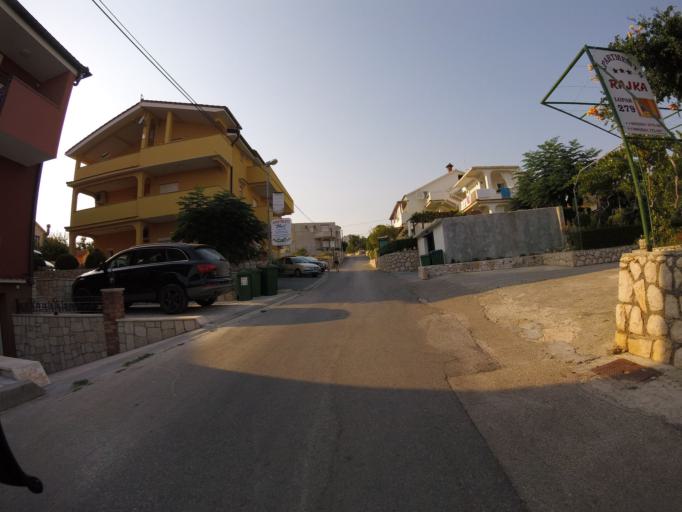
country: HR
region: Primorsko-Goranska
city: Lopar
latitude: 44.8317
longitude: 14.7302
